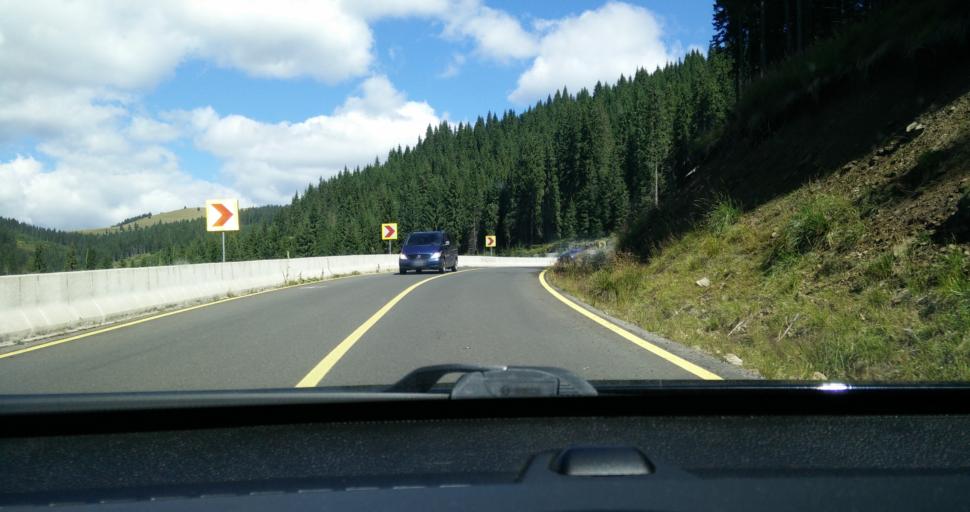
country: RO
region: Hunedoara
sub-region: Oras Petrila
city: Petrila
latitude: 45.4527
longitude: 23.6167
